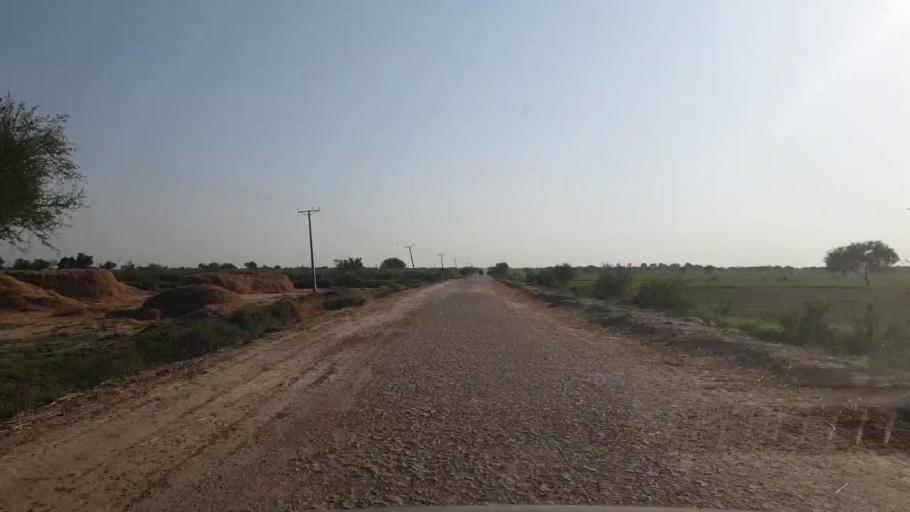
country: PK
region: Sindh
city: Talhar
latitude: 24.9396
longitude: 68.7516
